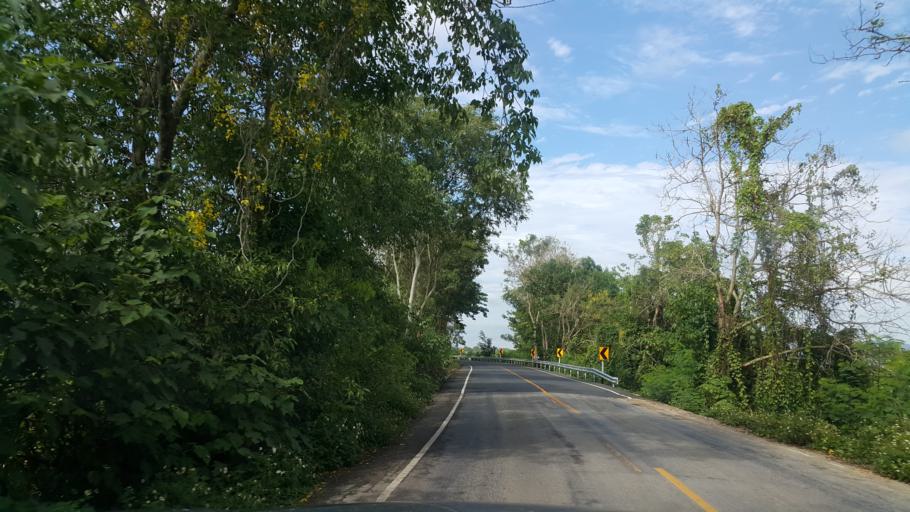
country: TH
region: Chiang Rai
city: Wiang Chai
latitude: 19.9364
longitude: 99.9159
